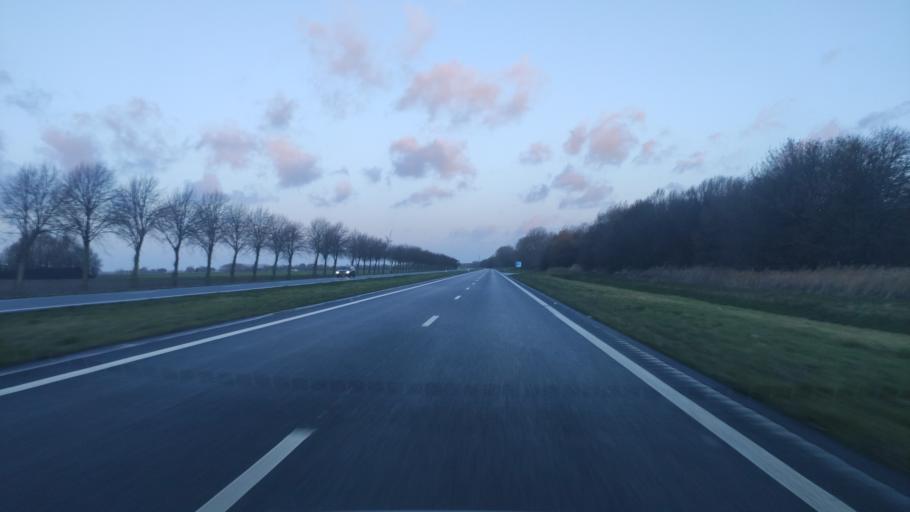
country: NL
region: Gelderland
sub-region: Gemeente Harderwijk
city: Harderwijk
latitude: 52.4213
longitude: 5.5794
